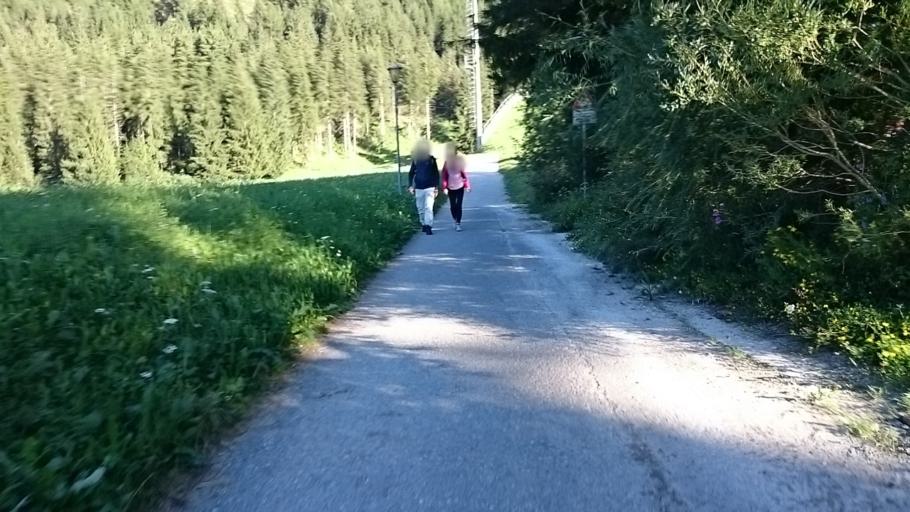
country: IT
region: Trentino-Alto Adige
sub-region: Bolzano
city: Dobbiaco
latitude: 46.7196
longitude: 12.2228
